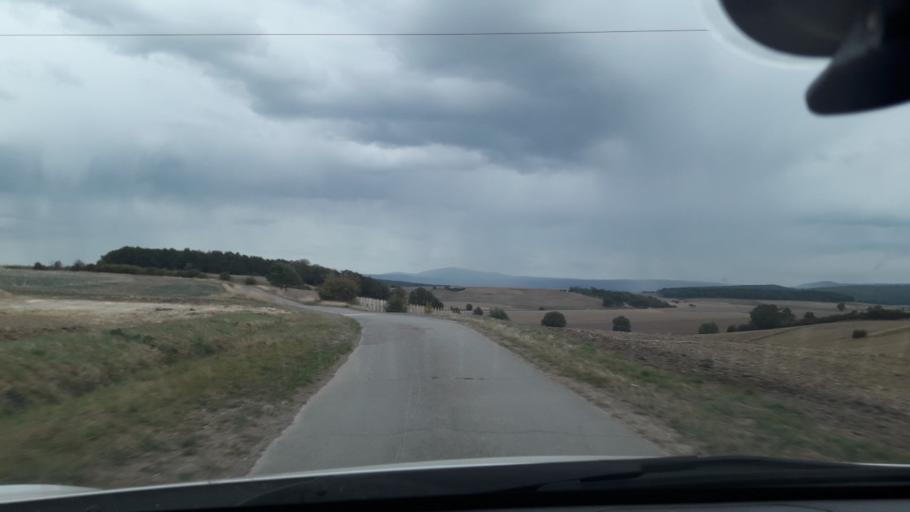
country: DE
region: Lower Saxony
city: Gielde
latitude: 52.0195
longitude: 10.4740
